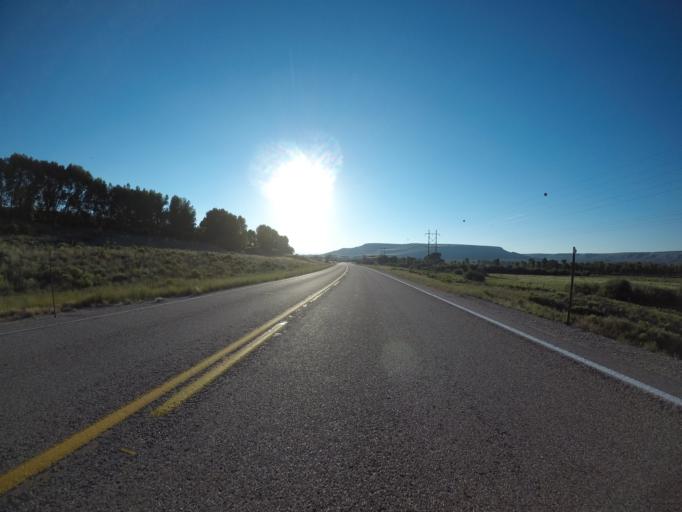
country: US
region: Wyoming
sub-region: Sublette County
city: Marbleton
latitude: 42.5698
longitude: -109.9548
